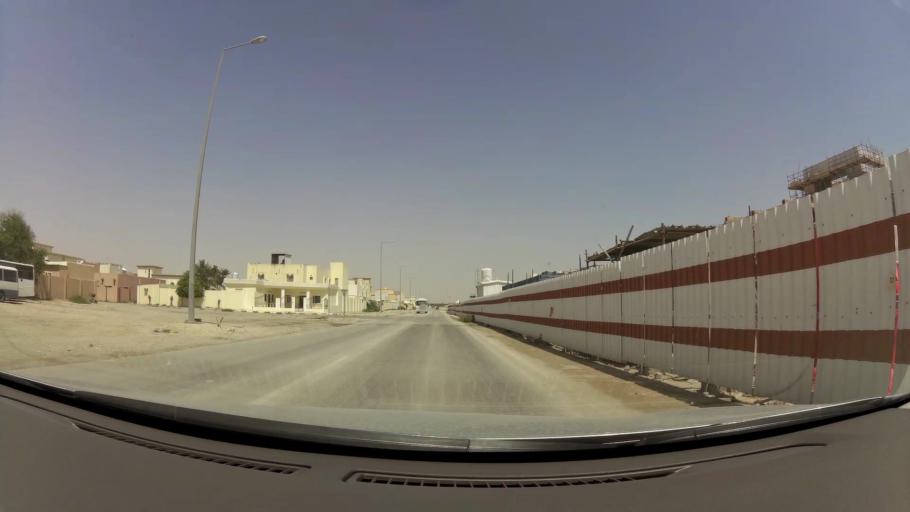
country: QA
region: Baladiyat Umm Salal
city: Umm Salal Muhammad
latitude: 25.3739
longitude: 51.4791
